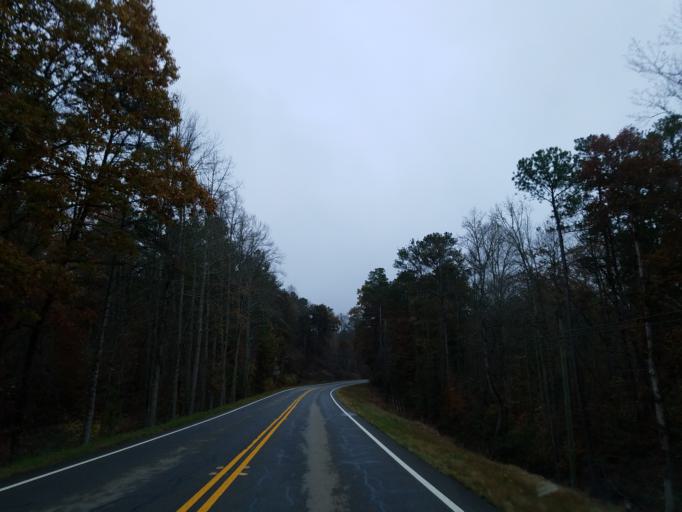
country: US
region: Georgia
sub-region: Pickens County
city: Jasper
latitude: 34.3849
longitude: -84.4735
